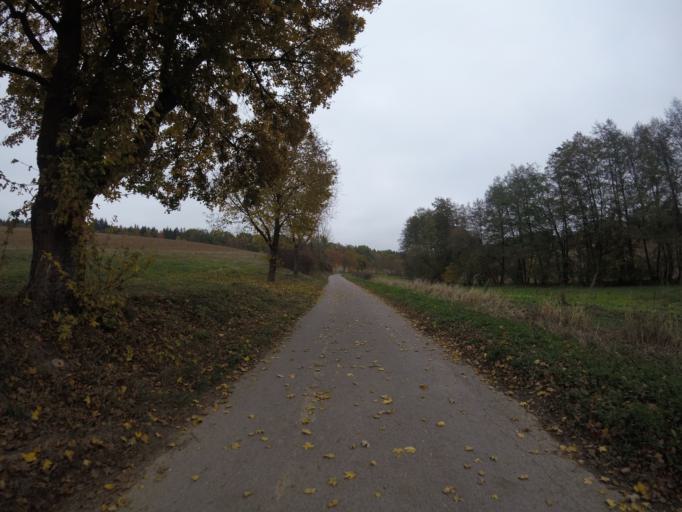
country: DE
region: Baden-Wuerttemberg
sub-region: Regierungsbezirk Stuttgart
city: Grossbottwar
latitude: 48.9741
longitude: 9.3126
